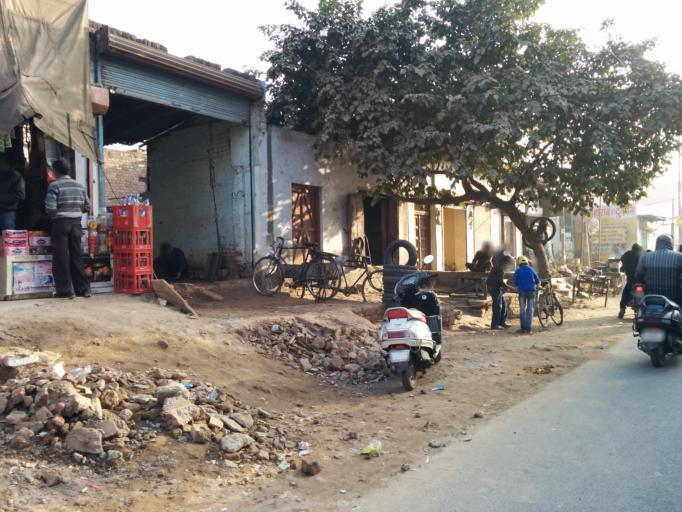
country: IN
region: Uttar Pradesh
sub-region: Mathura
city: Mathura
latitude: 27.5250
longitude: 77.6744
